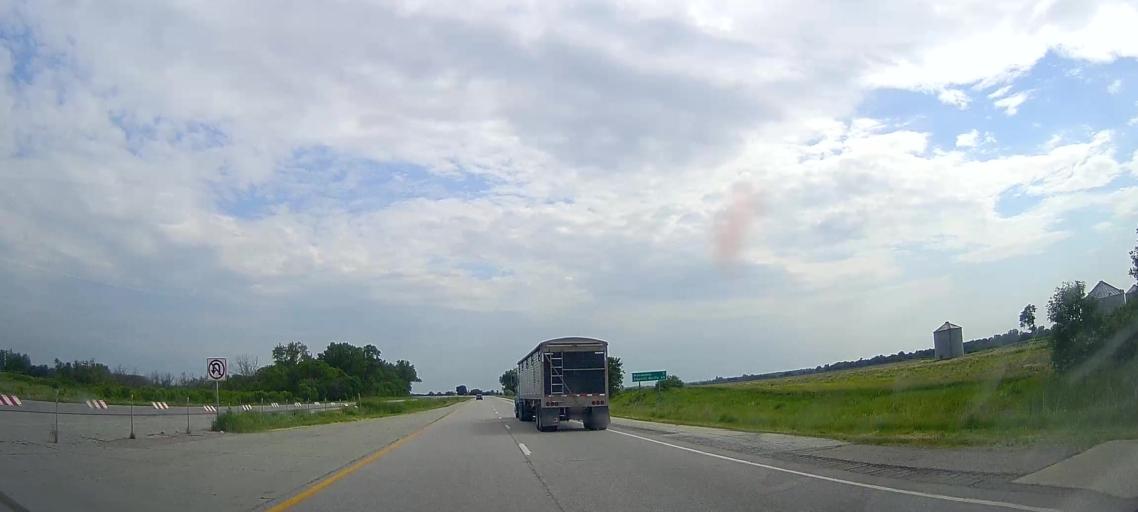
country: US
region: Nebraska
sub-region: Burt County
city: Tekamah
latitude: 41.7908
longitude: -96.0520
